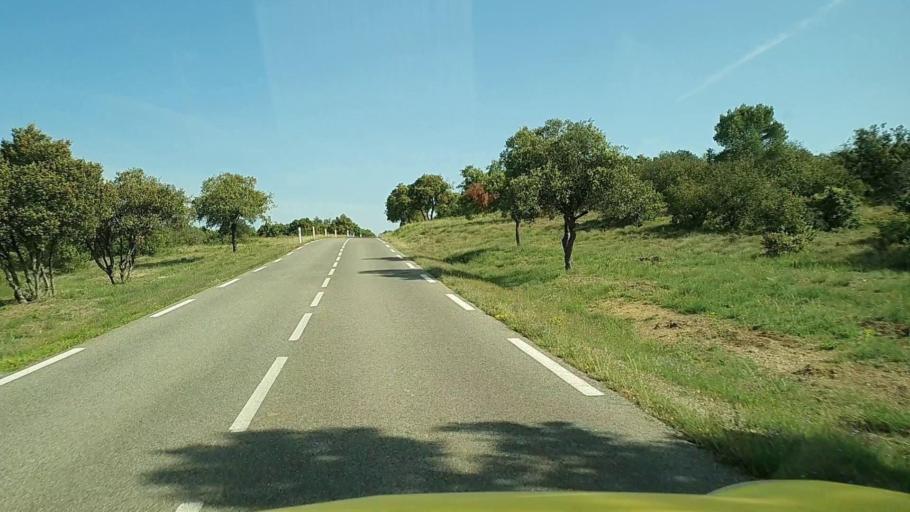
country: FR
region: Languedoc-Roussillon
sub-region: Departement du Gard
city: Montaren-et-Saint-Mediers
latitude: 44.0896
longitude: 4.3894
